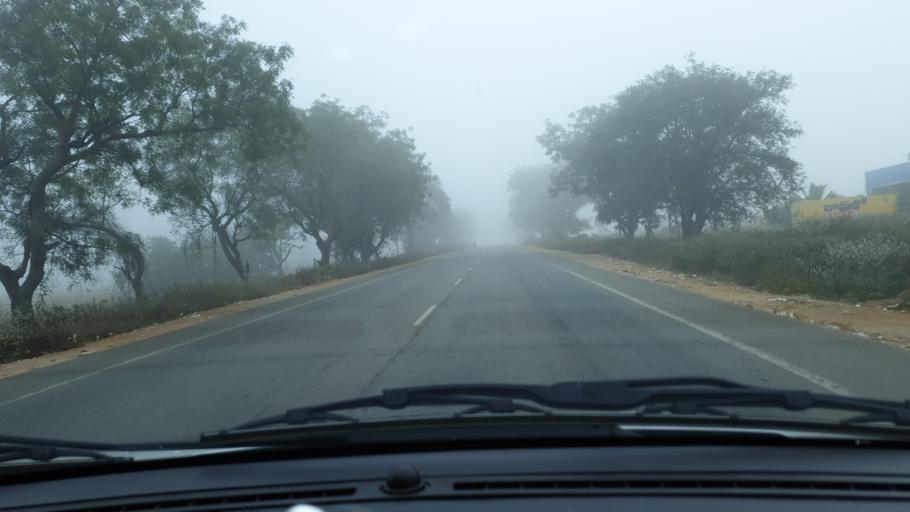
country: IN
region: Telangana
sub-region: Mahbubnagar
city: Nagar Karnul
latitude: 16.6646
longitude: 78.5529
